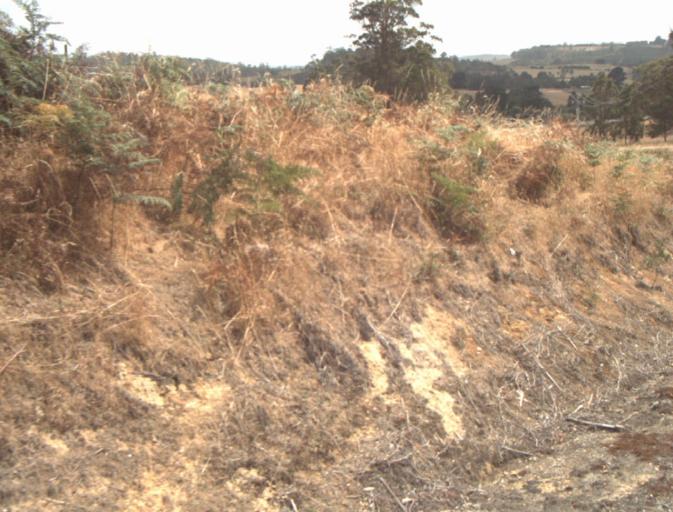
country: AU
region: Tasmania
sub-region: Launceston
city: Mayfield
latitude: -41.2027
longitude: 147.2176
